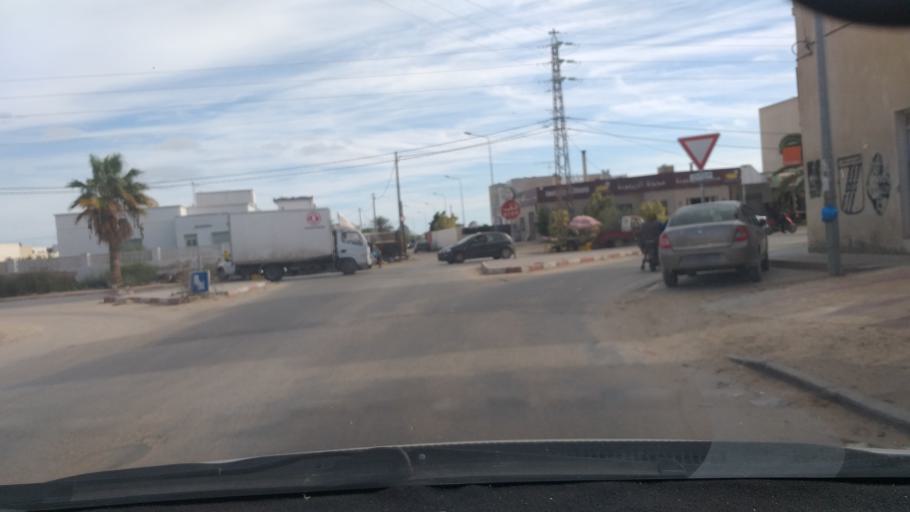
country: TN
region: Safaqis
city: Al Qarmadah
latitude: 34.7915
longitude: 10.8052
